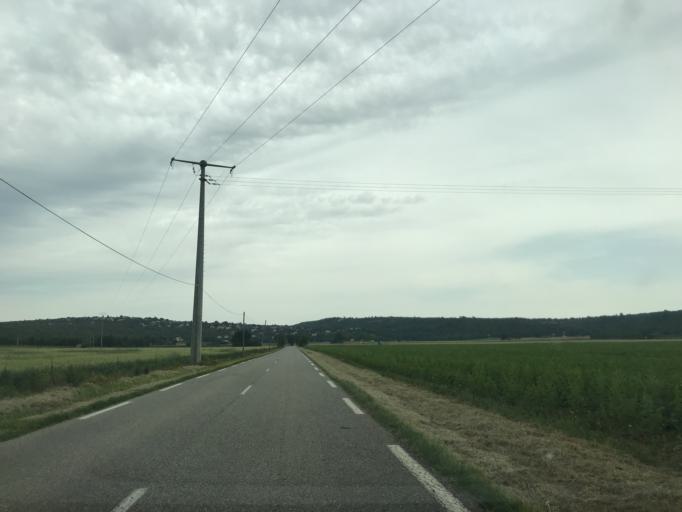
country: FR
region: Provence-Alpes-Cote d'Azur
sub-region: Departement du Var
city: Ginasservis
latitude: 43.6502
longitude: 5.8402
